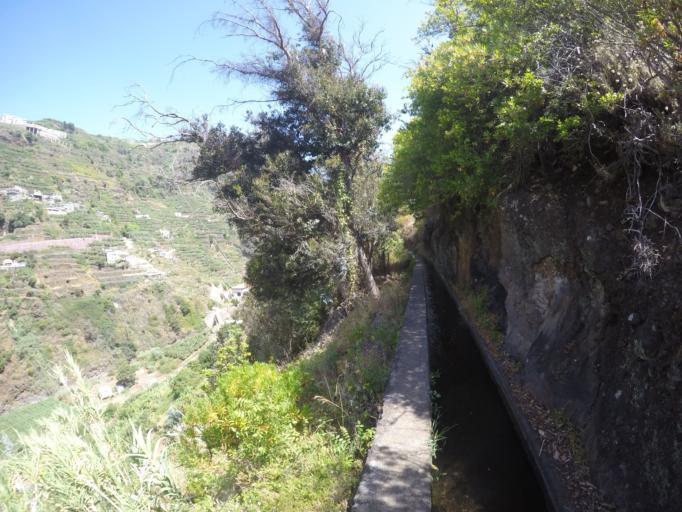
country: PT
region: Madeira
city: Camara de Lobos
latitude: 32.6638
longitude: -16.9591
